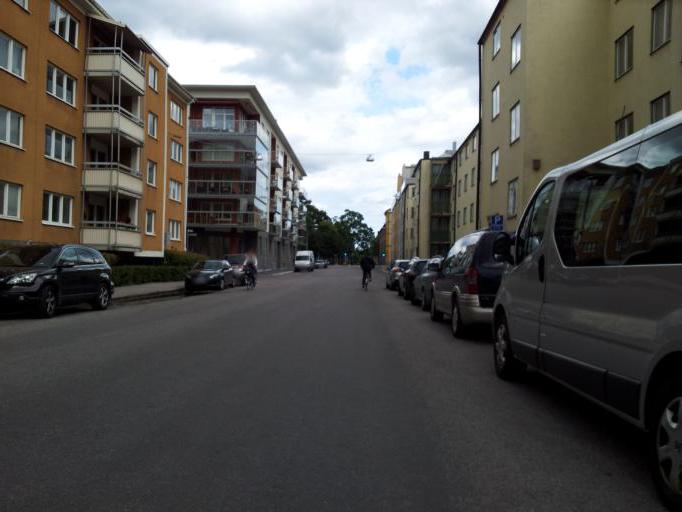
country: SE
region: Uppsala
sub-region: Uppsala Kommun
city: Uppsala
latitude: 59.8630
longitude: 17.6330
